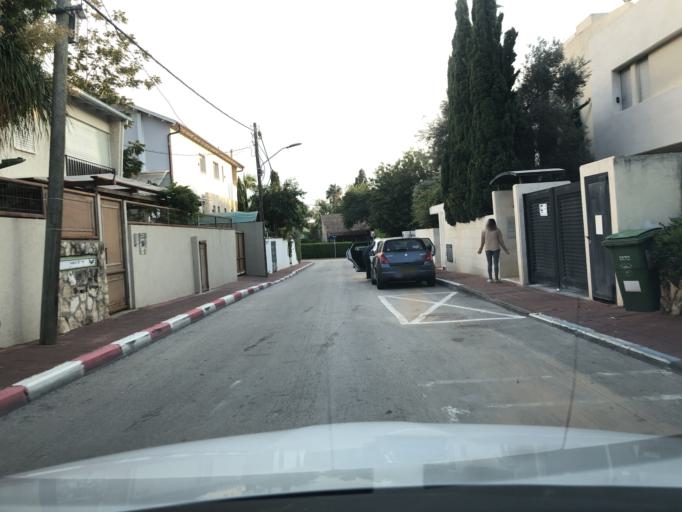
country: IL
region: Tel Aviv
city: Giv`atayim
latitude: 32.0579
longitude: 34.8232
